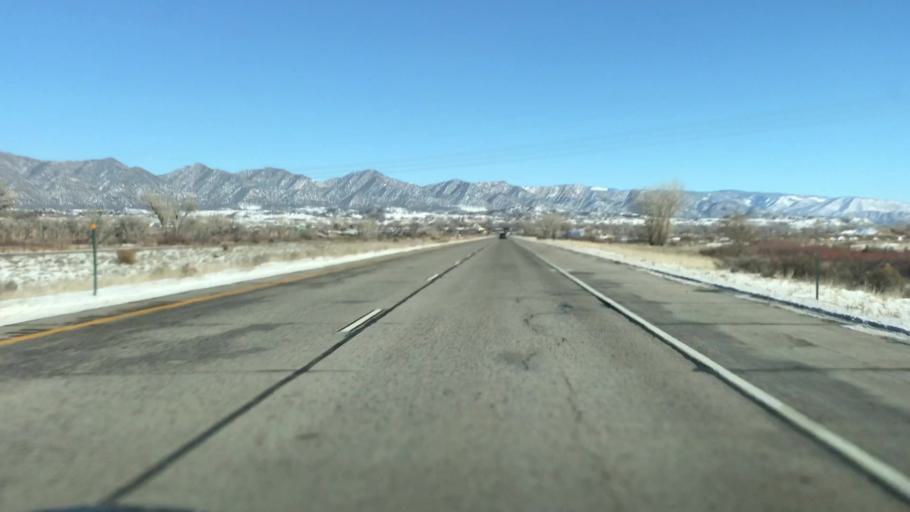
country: US
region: Colorado
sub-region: Garfield County
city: Silt
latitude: 39.5424
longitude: -107.6723
